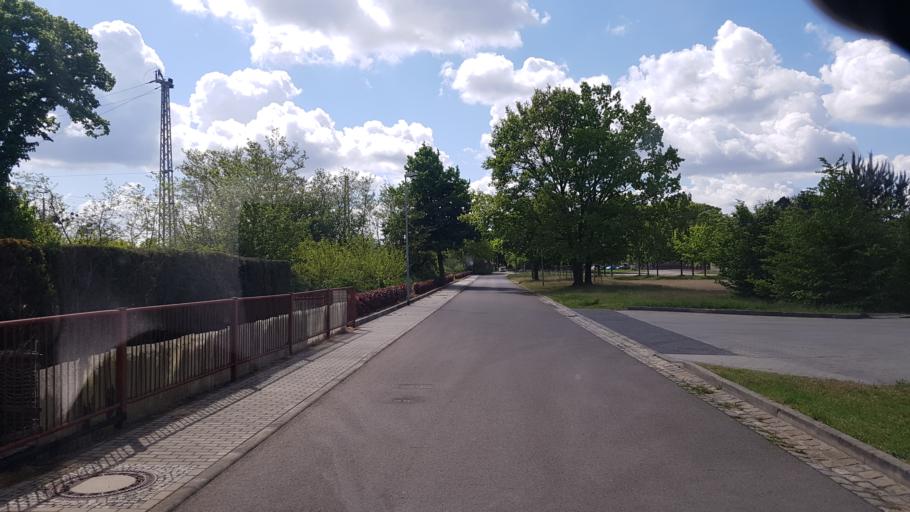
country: DE
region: Brandenburg
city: Grossraschen
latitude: 51.5910
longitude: 14.0145
